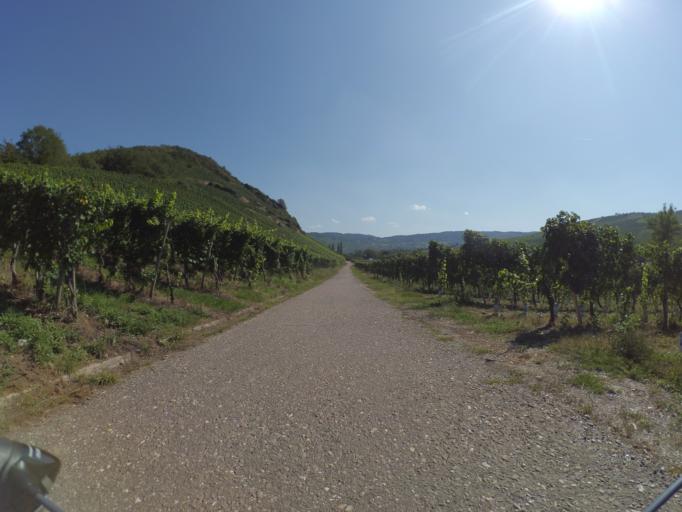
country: DE
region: Rheinland-Pfalz
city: Trittenheim
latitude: 49.8393
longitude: 6.8984
